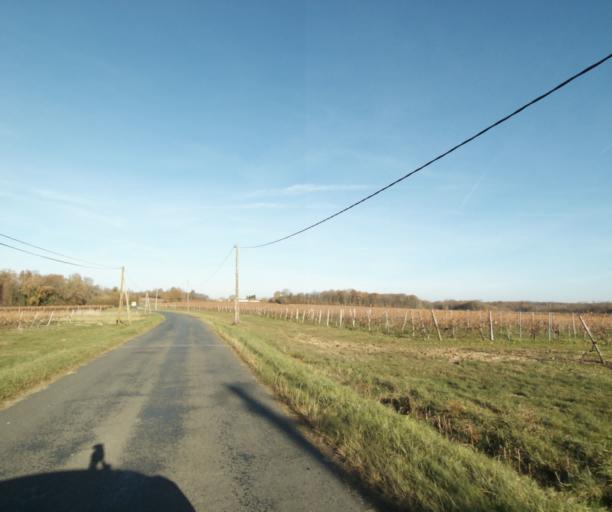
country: FR
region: Poitou-Charentes
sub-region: Departement de la Charente-Maritime
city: Cherac
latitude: 45.7194
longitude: -0.4533
